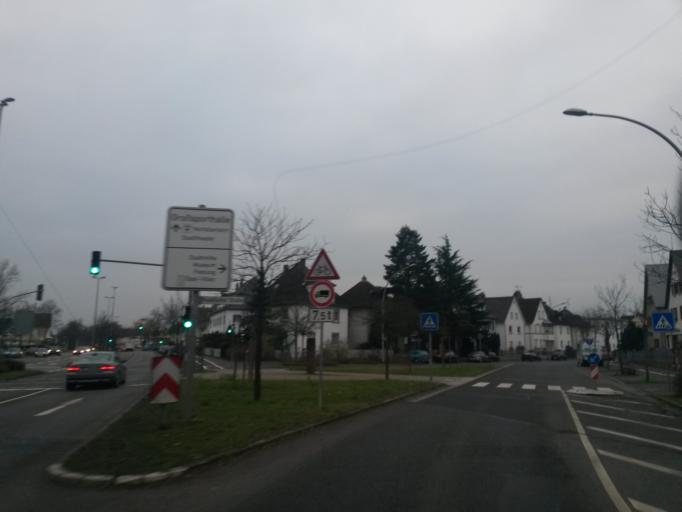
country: DE
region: Hesse
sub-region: Regierungsbezirk Darmstadt
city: Russelsheim
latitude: 49.9996
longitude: 8.4247
